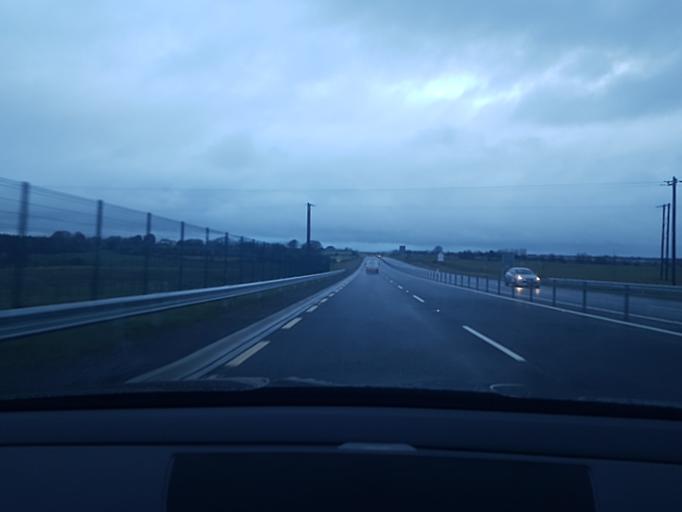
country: IE
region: Connaught
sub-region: County Galway
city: Tuam
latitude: 53.5276
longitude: -8.8693
